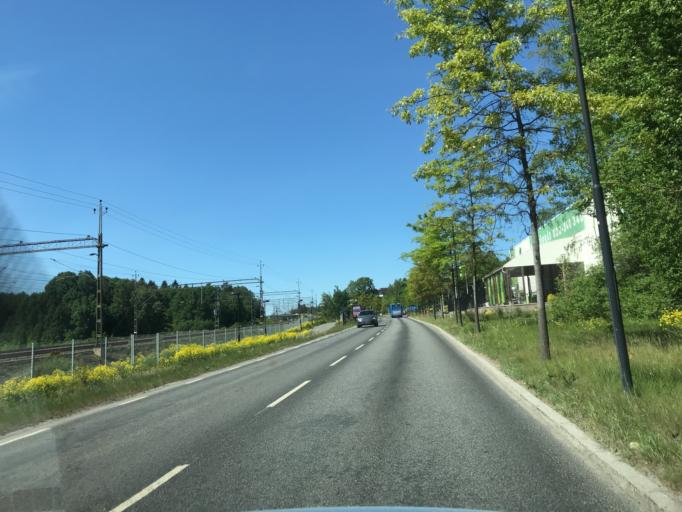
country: SE
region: Stockholm
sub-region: Solna Kommun
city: Rasunda
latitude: 59.3974
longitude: 17.9847
